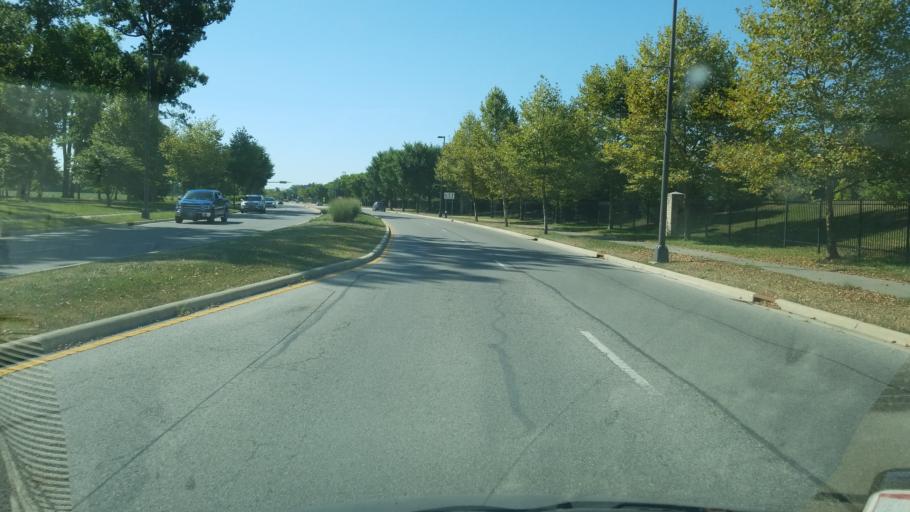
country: US
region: Ohio
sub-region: Franklin County
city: Hilliard
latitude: 40.0471
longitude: -83.1336
